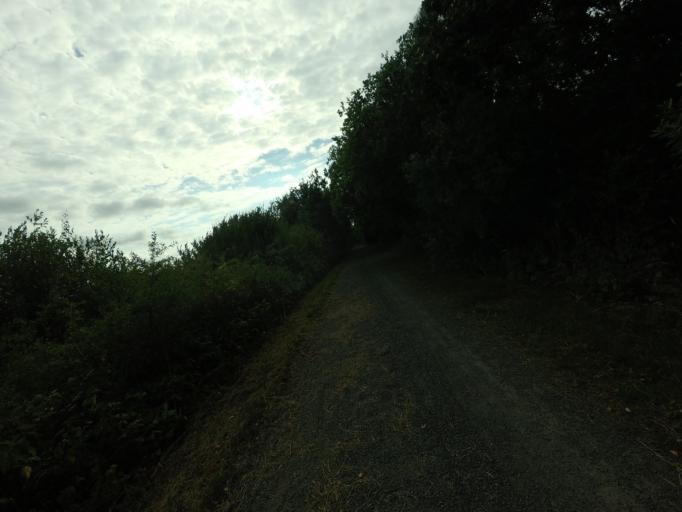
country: SE
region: Skane
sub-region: Helsingborg
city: Odakra
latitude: 56.1727
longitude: 12.7002
